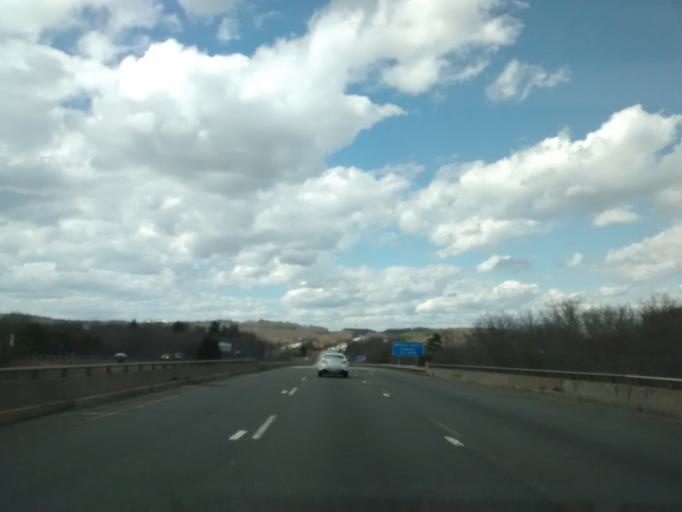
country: US
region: Massachusetts
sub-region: Worcester County
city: Cordaville
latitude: 42.2685
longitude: -71.5644
